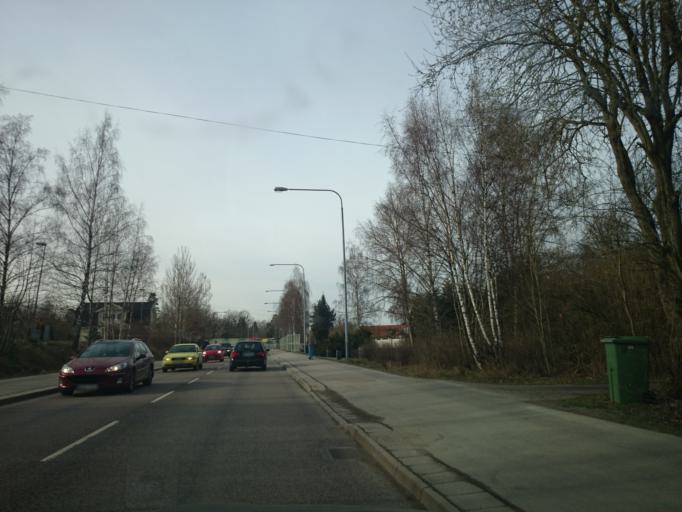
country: SE
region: Stockholm
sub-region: Huddinge Kommun
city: Huddinge
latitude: 59.2629
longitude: 17.9711
